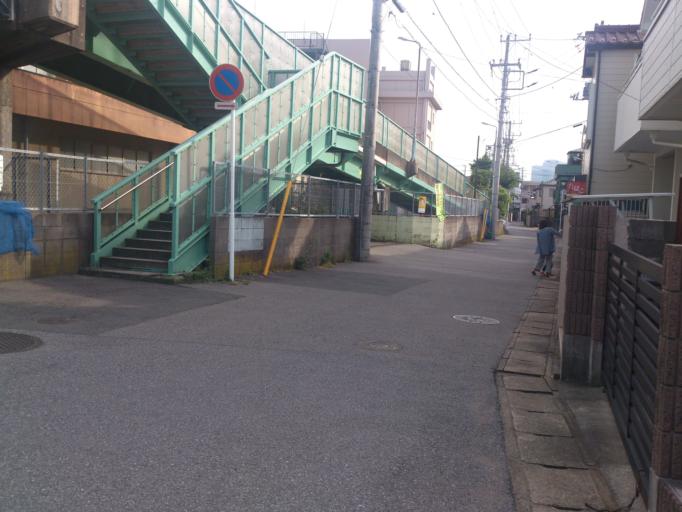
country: JP
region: Chiba
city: Funabashi
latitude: 35.6625
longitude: 140.0541
